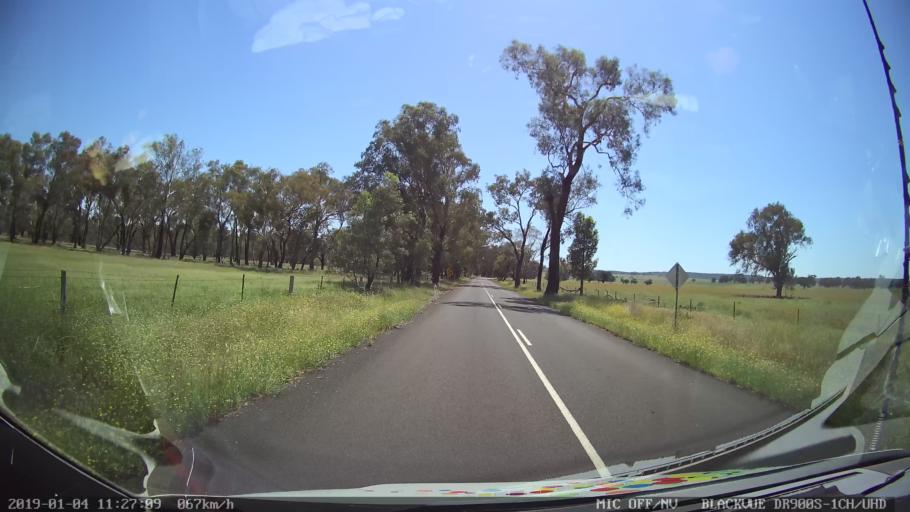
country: AU
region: New South Wales
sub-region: Cabonne
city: Molong
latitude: -33.1106
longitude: 148.7596
